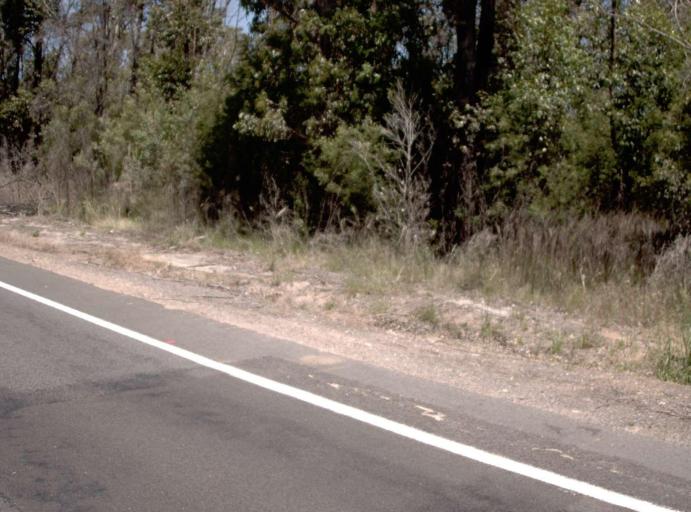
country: AU
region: Victoria
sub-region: East Gippsland
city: Lakes Entrance
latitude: -37.7548
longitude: 148.2978
